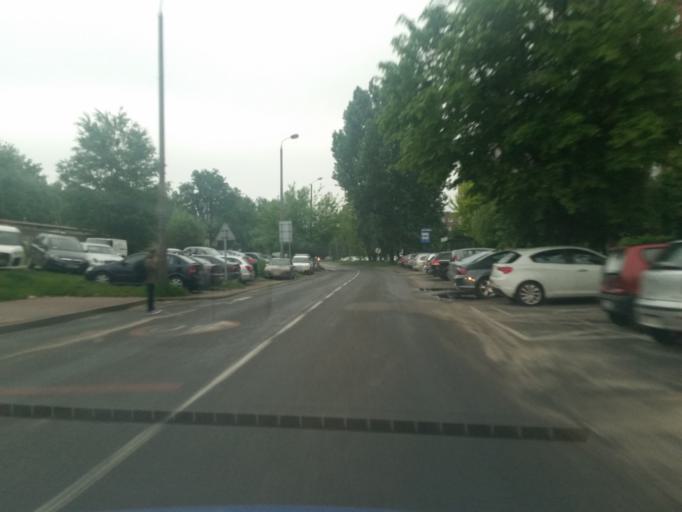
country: PL
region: Silesian Voivodeship
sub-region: Sosnowiec
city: Sosnowiec
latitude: 50.2687
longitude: 19.1243
